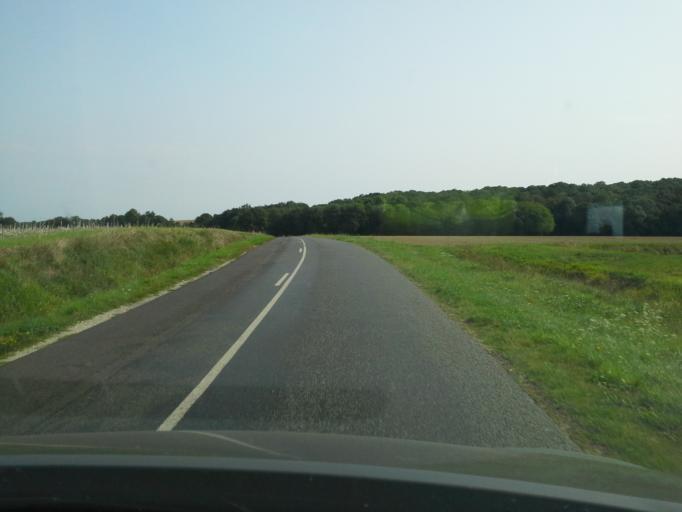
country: FR
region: Centre
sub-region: Departement du Loir-et-Cher
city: La Ville-aux-Clercs
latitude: 47.9041
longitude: 1.0434
